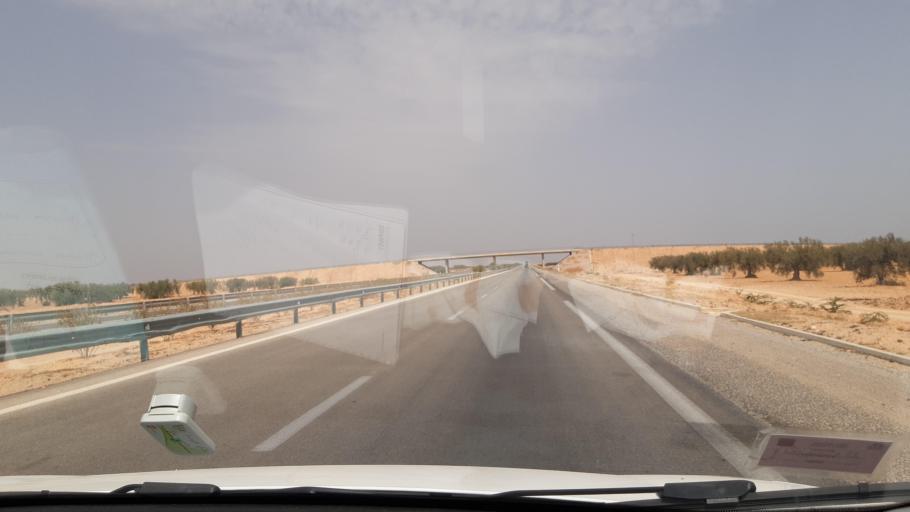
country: TN
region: Safaqis
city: Bi'r `Ali Bin Khalifah
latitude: 34.5746
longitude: 10.3879
